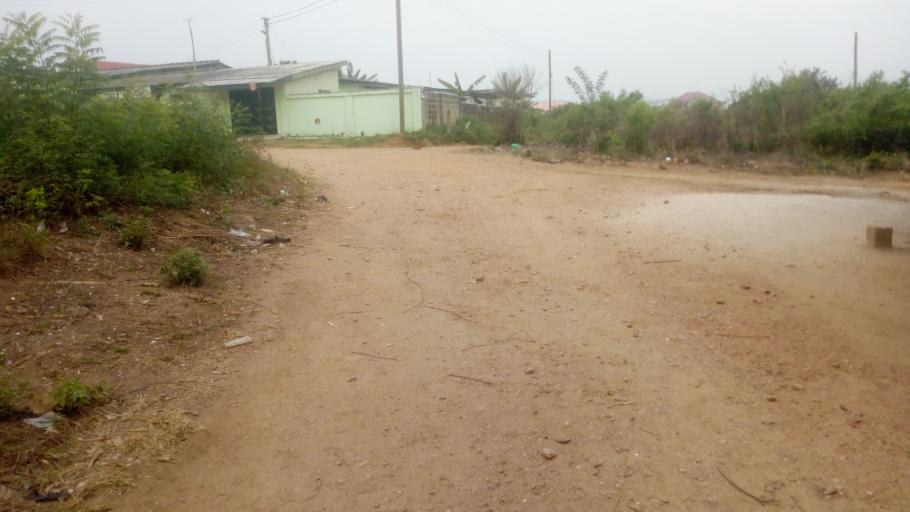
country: GH
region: Central
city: Winneba
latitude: 5.3596
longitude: -0.6260
